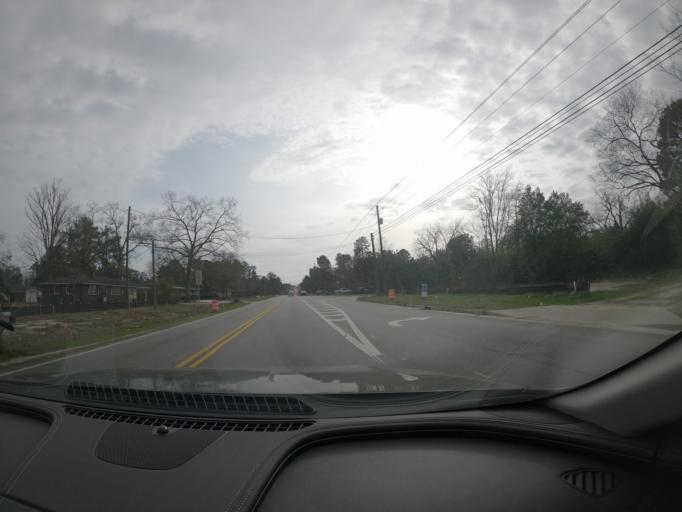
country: US
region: Georgia
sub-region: Columbia County
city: Martinez
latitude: 33.5049
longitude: -82.1064
